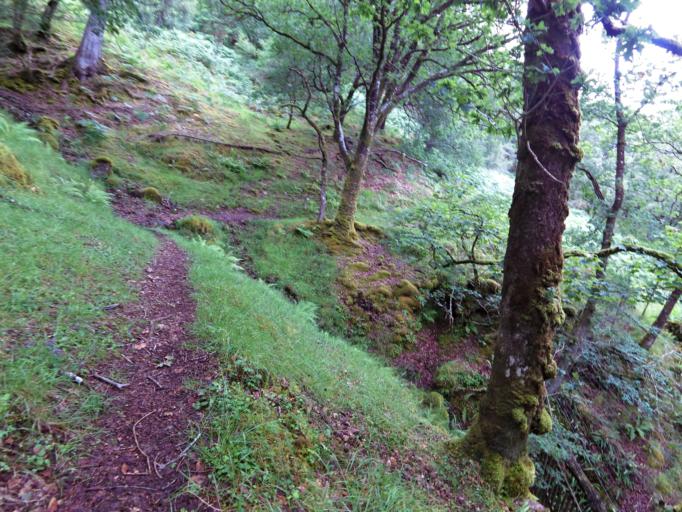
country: GB
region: Scotland
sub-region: Highland
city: Fort William
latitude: 56.8288
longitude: -5.1280
